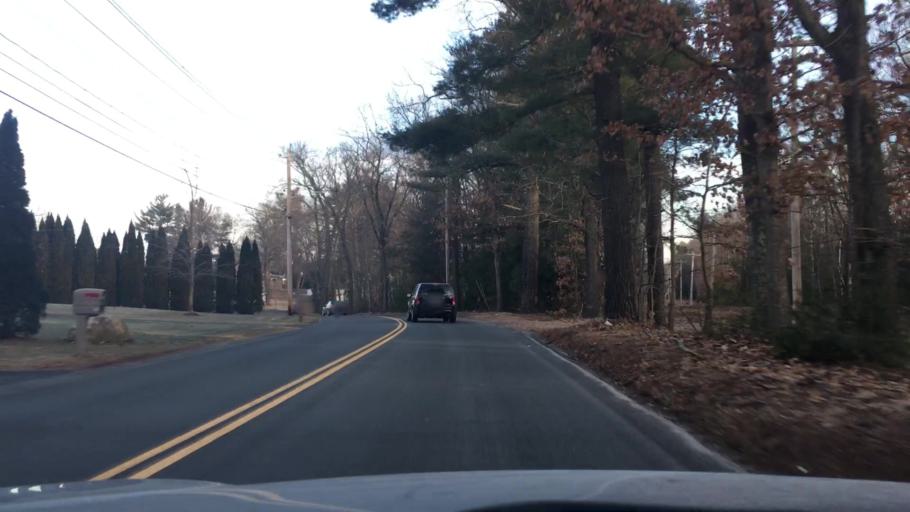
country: US
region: Massachusetts
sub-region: Hampden County
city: Westfield
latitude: 42.1309
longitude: -72.7225
